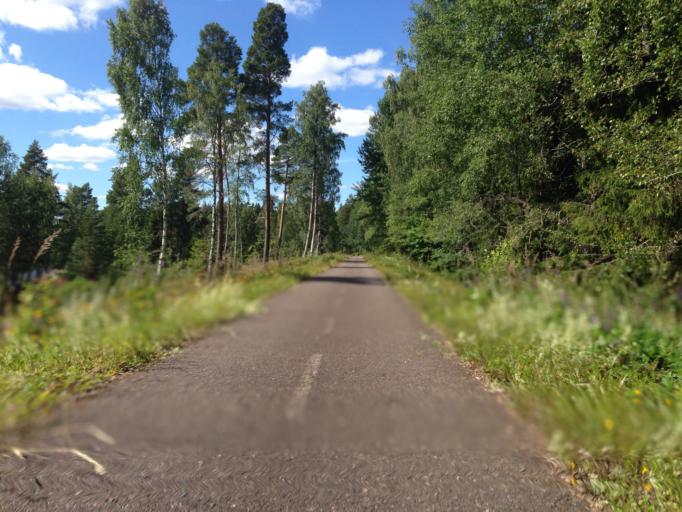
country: SE
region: Dalarna
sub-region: Ludvika Kommun
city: Ludvika
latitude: 60.1985
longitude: 15.0838
